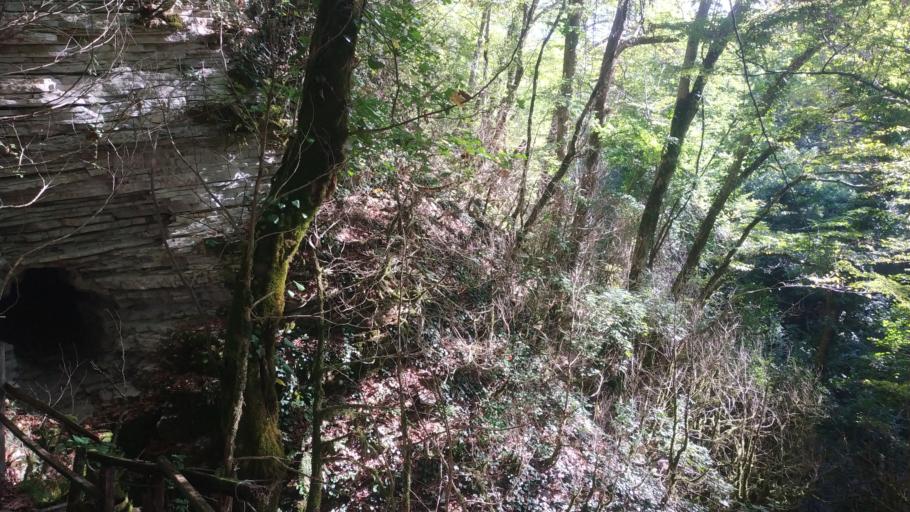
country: RU
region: Krasnodarskiy
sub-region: Sochi City
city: Lazarevskoye
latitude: 43.9835
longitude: 39.4095
